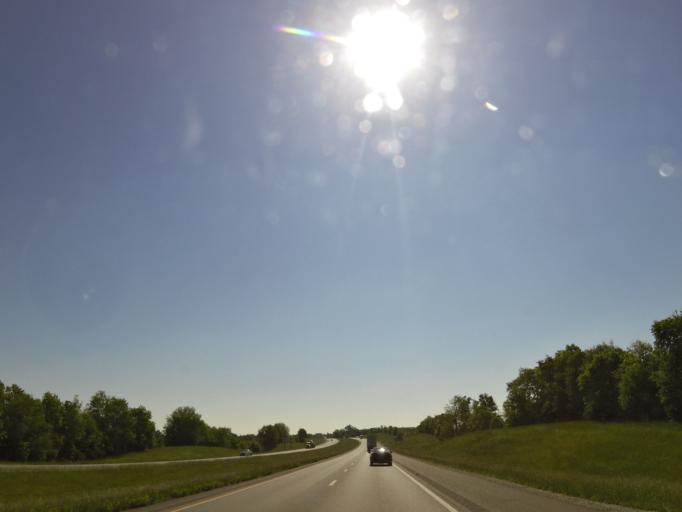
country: US
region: Kentucky
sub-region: Woodford County
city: Midway
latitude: 38.1592
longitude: -84.6642
